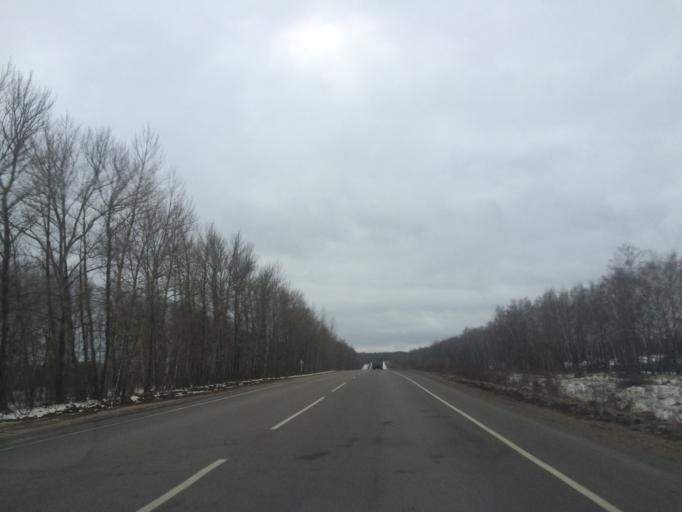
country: RU
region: Tula
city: Pervomayskiy
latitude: 54.1403
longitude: 37.3814
